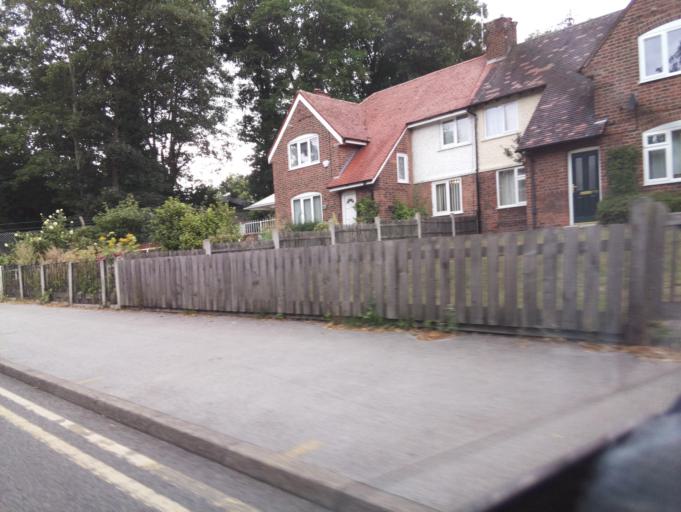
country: GB
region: England
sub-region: Nottinghamshire
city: Arnold
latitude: 52.9909
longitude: -1.1399
